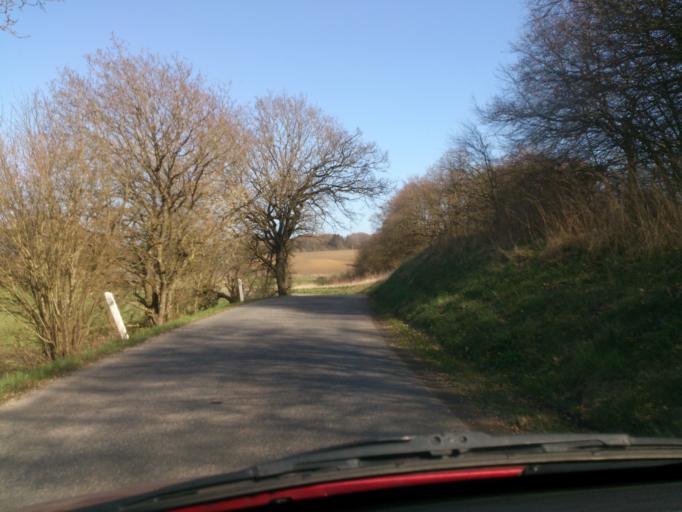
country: DK
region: Central Jutland
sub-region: Favrskov Kommune
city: Ulstrup
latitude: 56.4776
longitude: 9.7872
